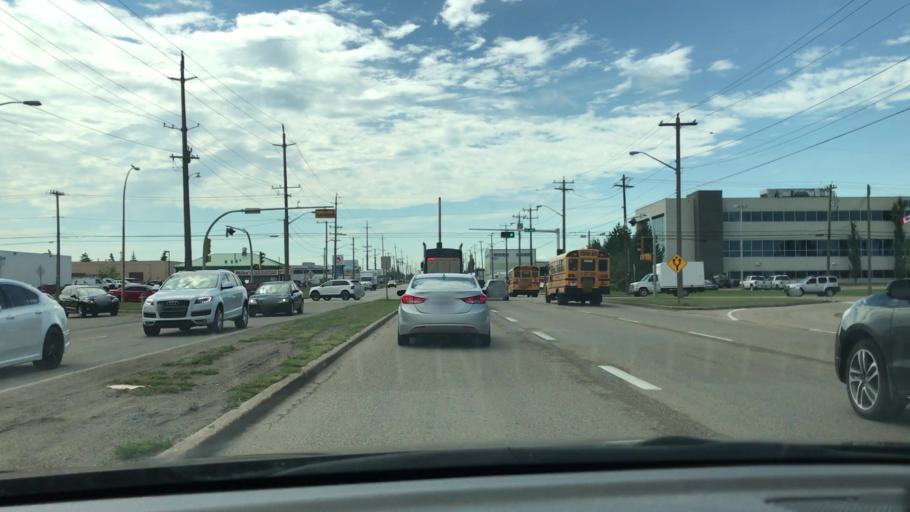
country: CA
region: Alberta
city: Edmonton
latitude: 53.5131
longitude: -113.4184
